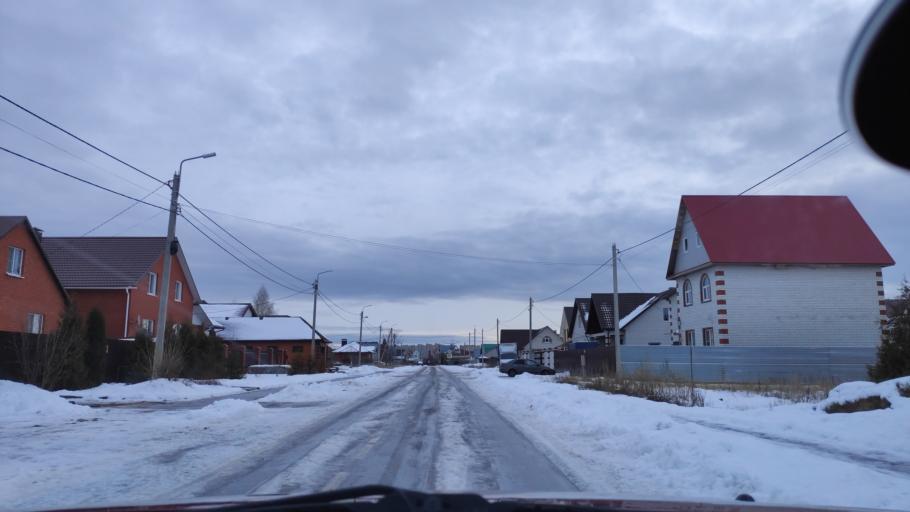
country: RU
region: Tambov
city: Komsomolets
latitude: 52.7617
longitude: 41.3652
